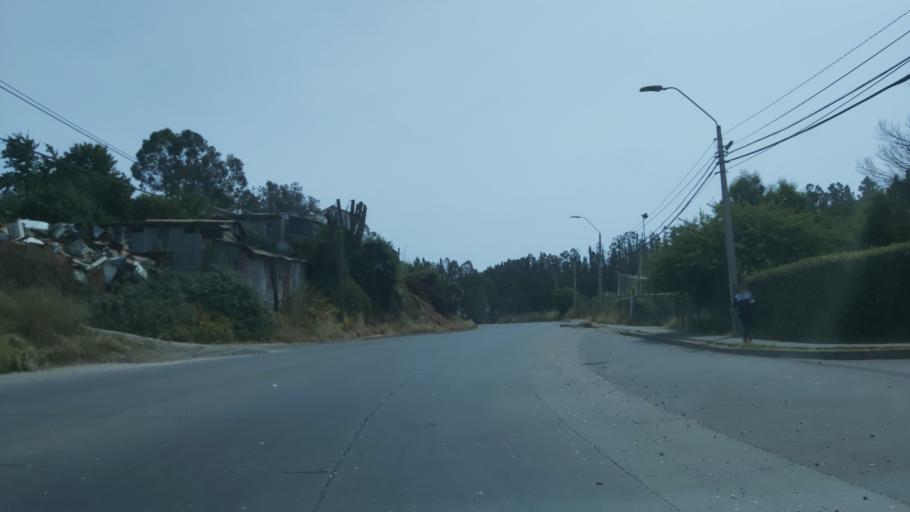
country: CL
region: Maule
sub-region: Provincia de Talca
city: Constitucion
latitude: -35.3376
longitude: -72.4179
